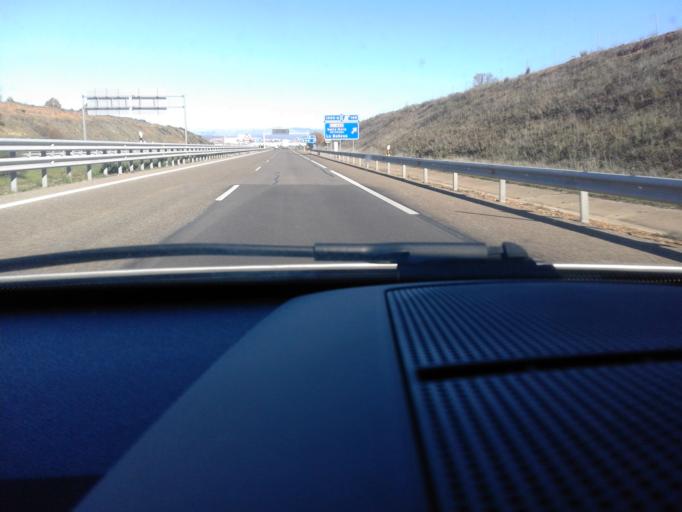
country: ES
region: Castille and Leon
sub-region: Provincia de Leon
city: Onzonilla
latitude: 42.5153
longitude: -5.5950
